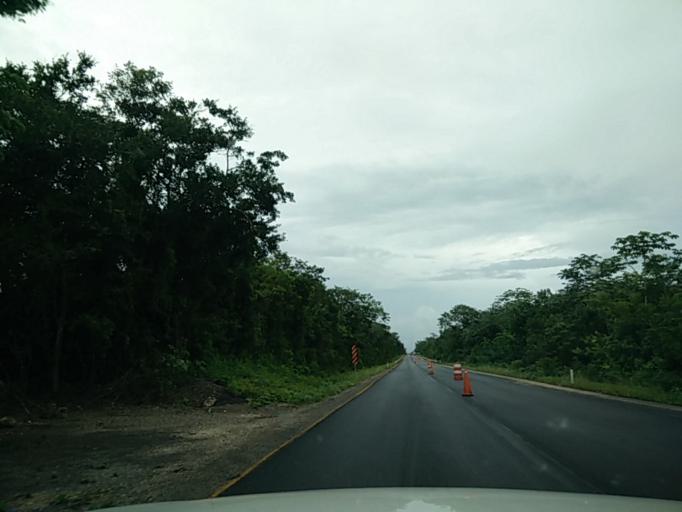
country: MX
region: Quintana Roo
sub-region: Lazaro Cardenas
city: El Tintal
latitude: 20.8974
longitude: -87.4858
